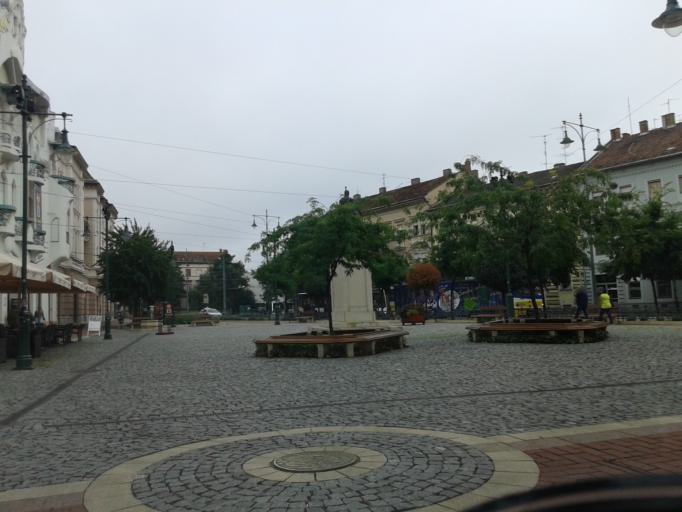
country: HU
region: Csongrad
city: Szeged
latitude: 46.2519
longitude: 20.1455
